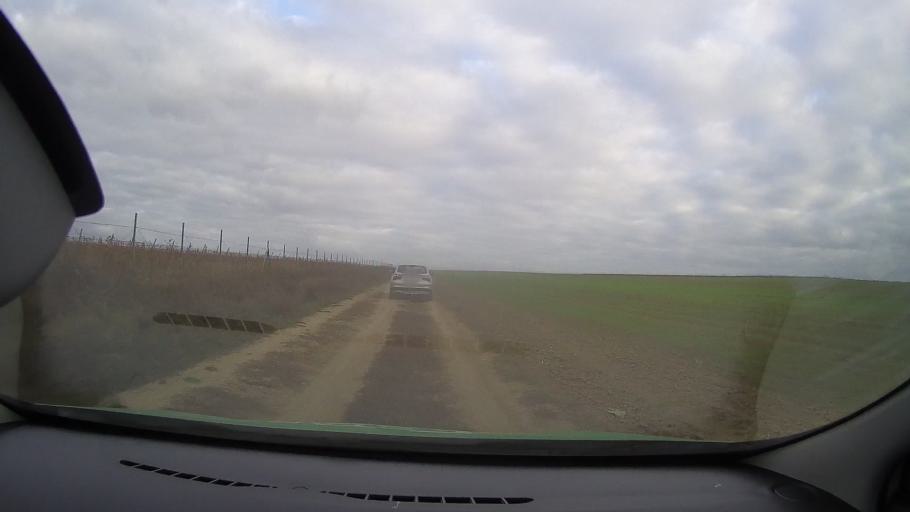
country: RO
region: Tulcea
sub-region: Comuna Jurilovca
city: Jurilovca
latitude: 44.7667
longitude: 28.9069
